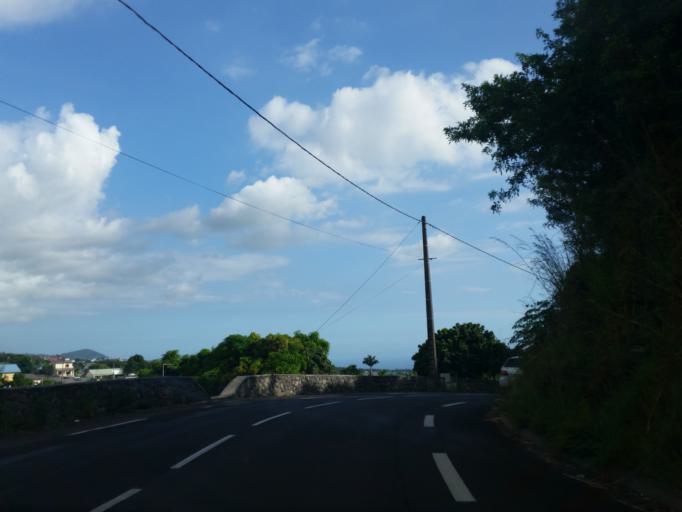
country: RE
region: Reunion
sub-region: Reunion
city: L'Entre-Deux
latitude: -21.2480
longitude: 55.4767
